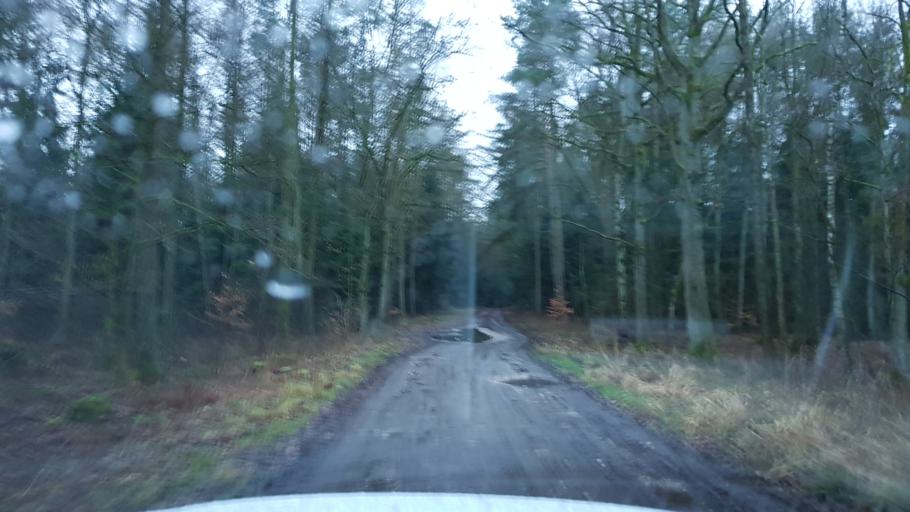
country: PL
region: West Pomeranian Voivodeship
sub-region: Powiat goleniowski
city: Osina
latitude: 53.5755
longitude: 15.0598
